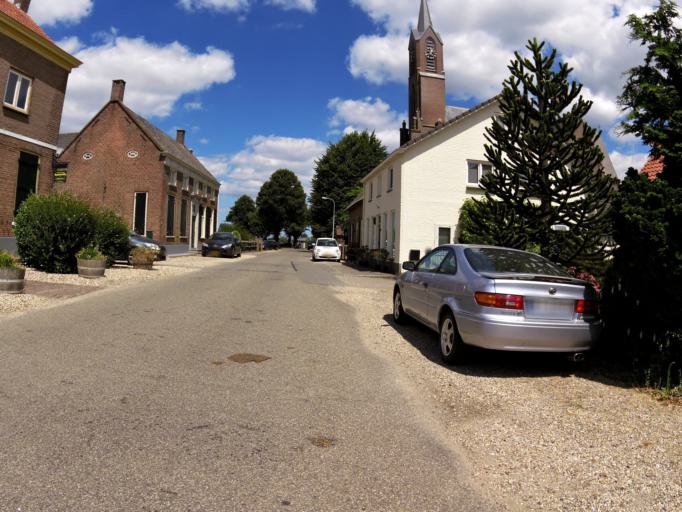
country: NL
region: Gelderland
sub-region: Gemeente Maasdriel
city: Heerewaarden
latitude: 51.7880
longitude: 5.3391
